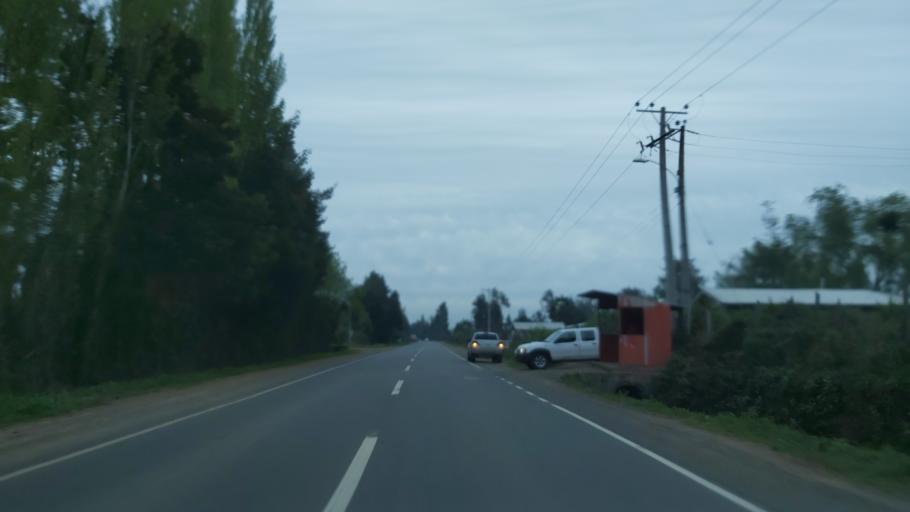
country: CL
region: Maule
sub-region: Provincia de Linares
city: Colbun
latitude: -35.7323
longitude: -71.4884
